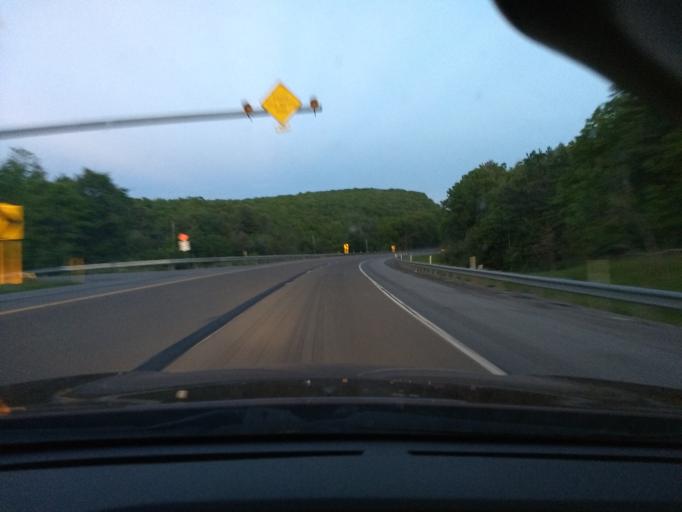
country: US
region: Pennsylvania
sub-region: Lycoming County
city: Jersey Shore
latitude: 41.0624
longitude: -77.2149
